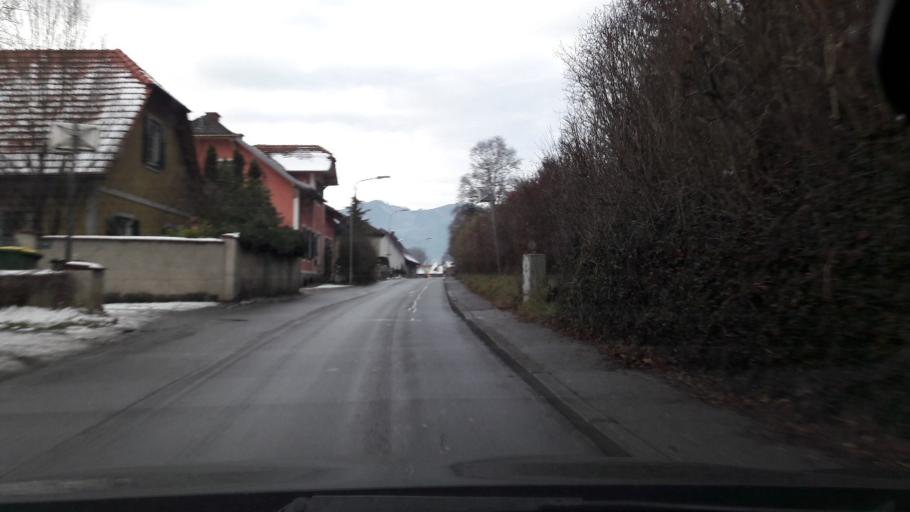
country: AT
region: Styria
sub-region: Politischer Bezirk Graz-Umgebung
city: Gratwein
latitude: 47.1302
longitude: 15.3129
